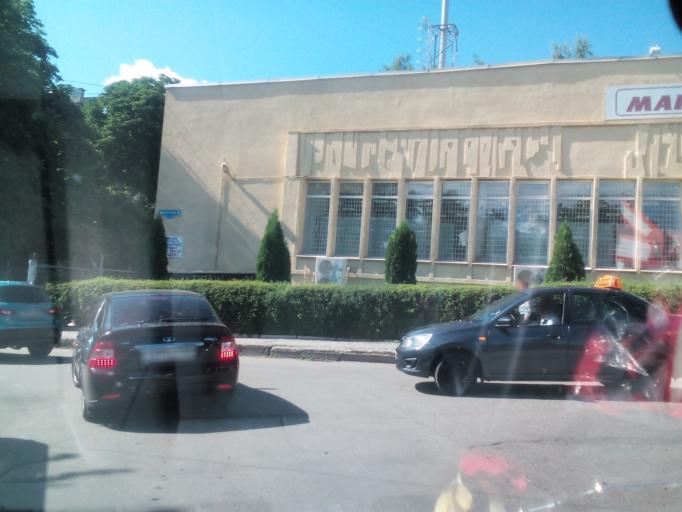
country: RU
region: Stavropol'skiy
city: Pyatigorsk
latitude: 44.0509
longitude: 43.0661
